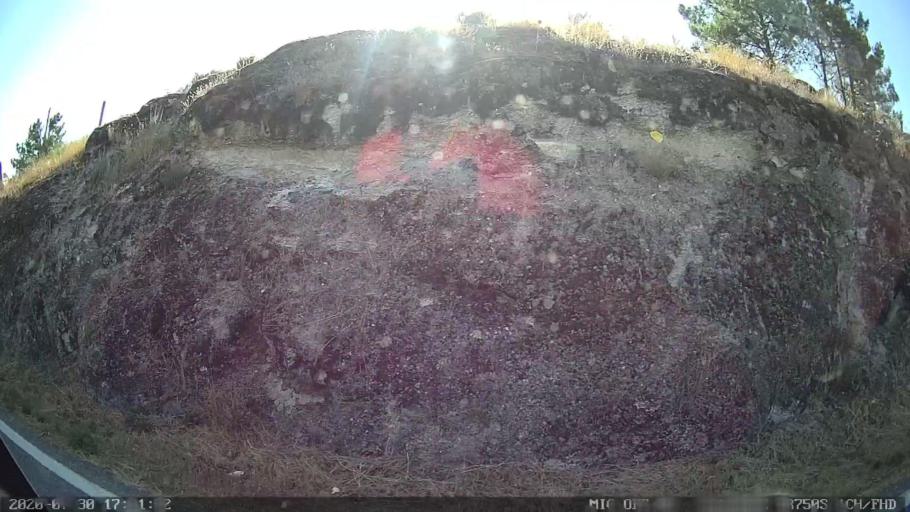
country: PT
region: Vila Real
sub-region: Sabrosa
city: Sabrosa
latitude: 41.2995
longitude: -7.4758
